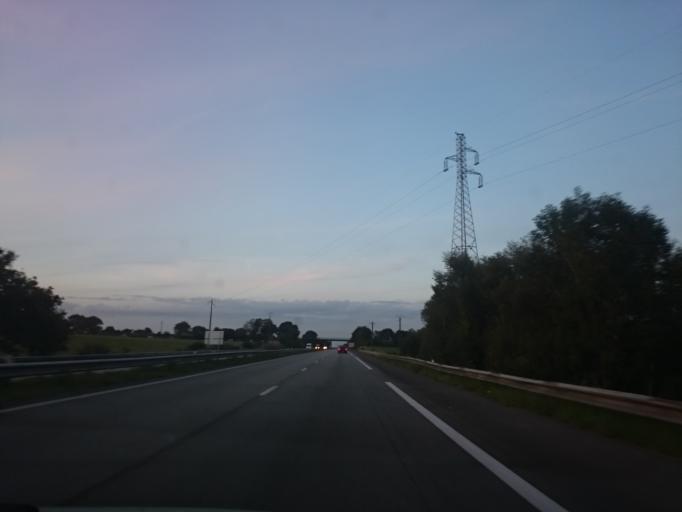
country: FR
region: Brittany
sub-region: Departement du Finistere
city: Briec
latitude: 48.1085
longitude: -4.0281
